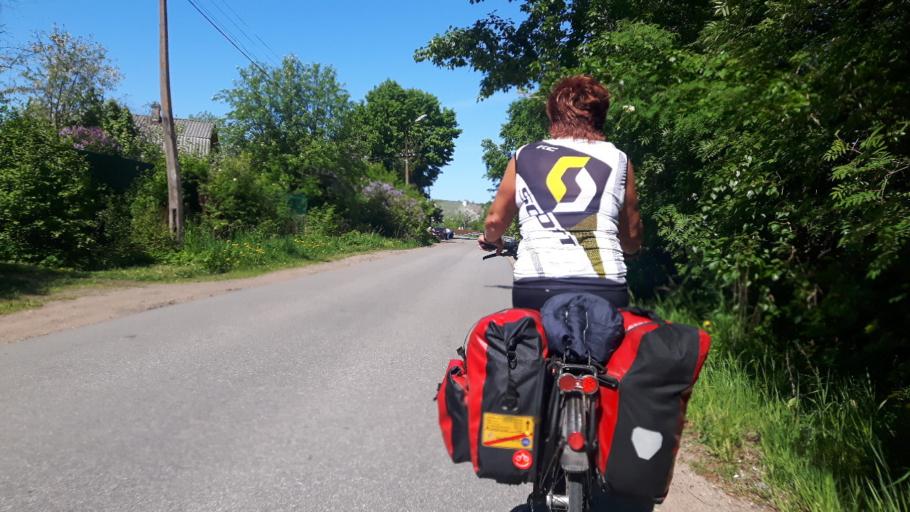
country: RU
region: Leningrad
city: Lebyazh'ye
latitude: 59.9713
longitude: 29.3829
